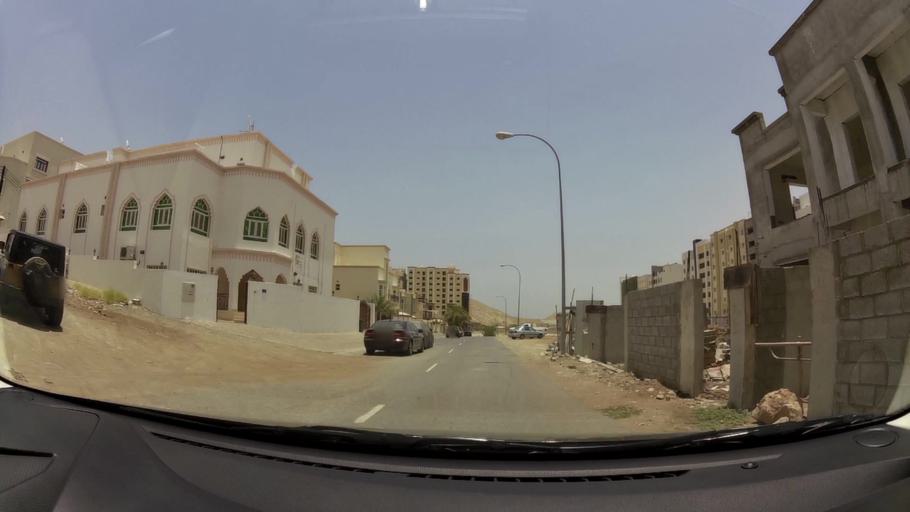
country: OM
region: Muhafazat Masqat
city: Bawshar
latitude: 23.5619
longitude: 58.4181
